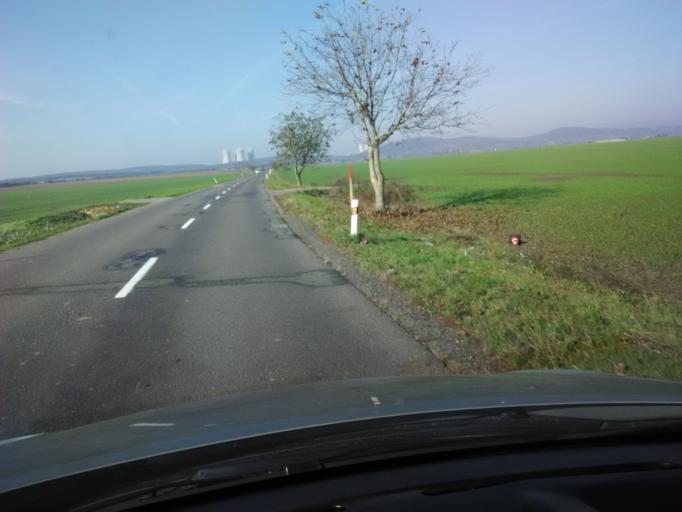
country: SK
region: Nitriansky
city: Tlmace
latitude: 48.2167
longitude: 18.5051
